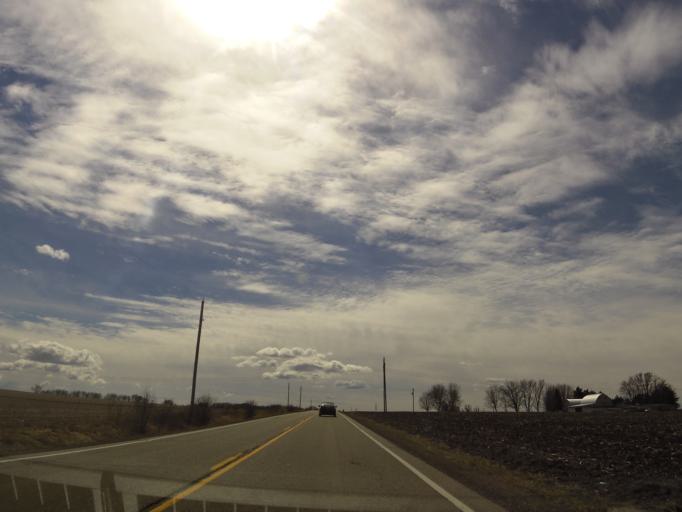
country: US
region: Minnesota
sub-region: Washington County
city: Afton
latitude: 44.8855
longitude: -92.8625
